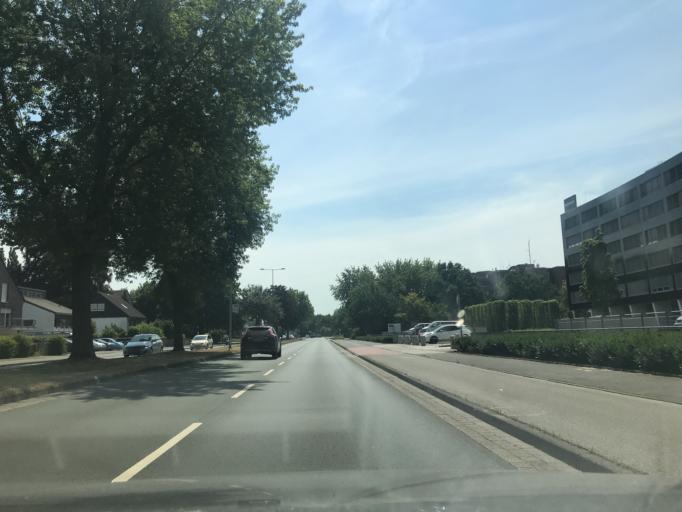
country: DE
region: North Rhine-Westphalia
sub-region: Regierungsbezirk Dusseldorf
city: Wesel
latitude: 51.6674
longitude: 6.6093
